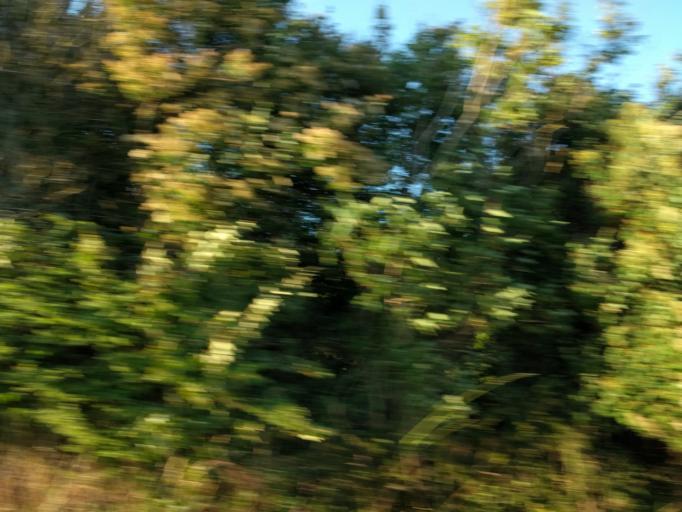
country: DK
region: South Denmark
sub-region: Kerteminde Kommune
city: Munkebo
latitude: 55.6075
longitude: 10.6196
